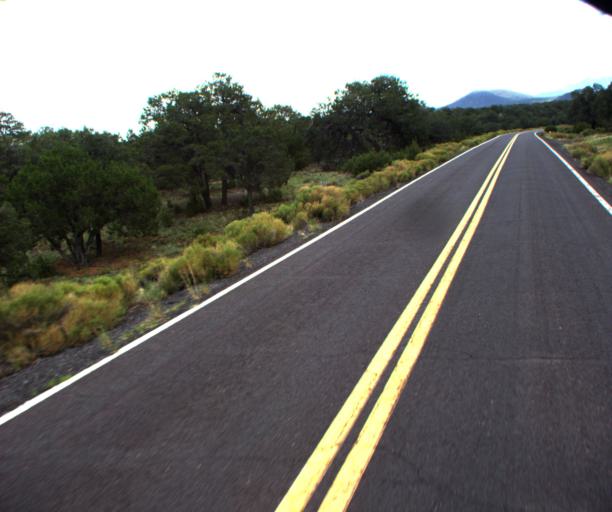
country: US
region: Arizona
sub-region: Coconino County
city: Parks
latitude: 35.5442
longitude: -111.8566
